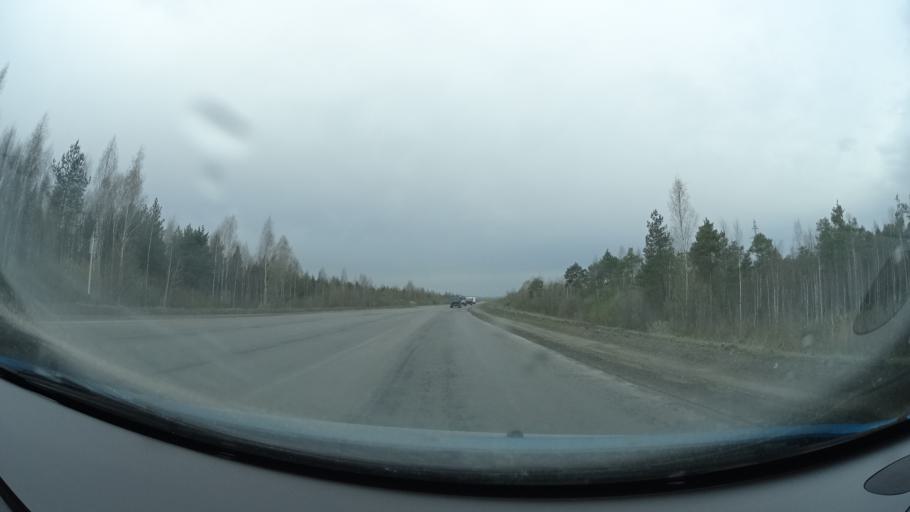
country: RU
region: Perm
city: Krasnokamsk
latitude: 58.0872
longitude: 55.7048
